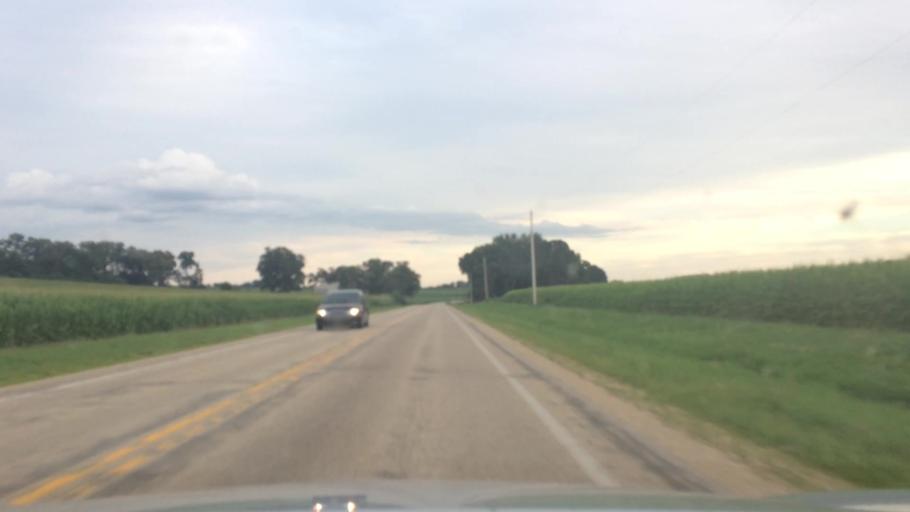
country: US
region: Wisconsin
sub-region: Dane County
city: Waunakee
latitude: 43.2193
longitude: -89.5462
